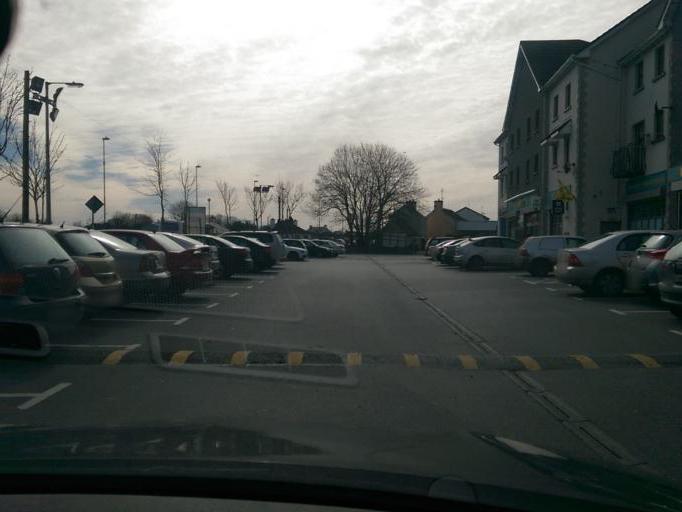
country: IE
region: Connaught
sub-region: County Galway
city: Claregalway
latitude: 53.3429
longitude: -8.9440
